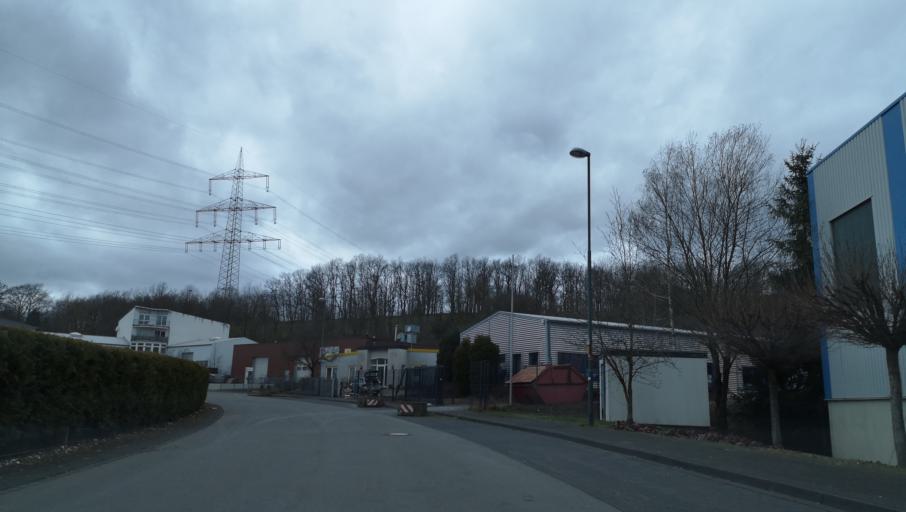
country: DE
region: North Rhine-Westphalia
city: Huckeswagen
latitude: 51.1342
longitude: 7.3343
